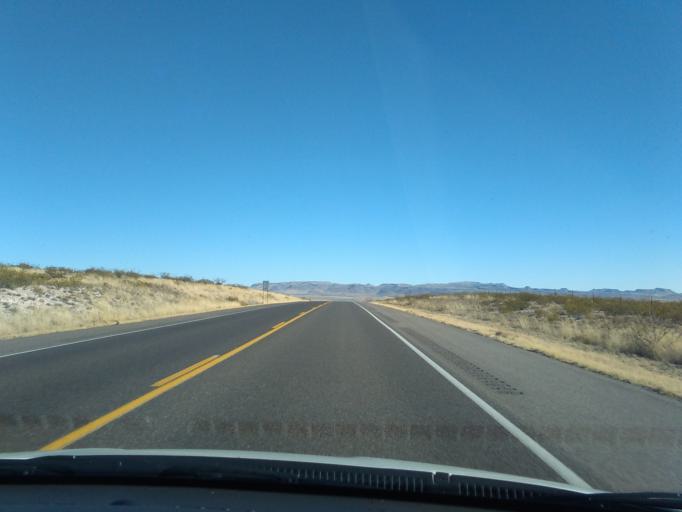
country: US
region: New Mexico
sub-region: Dona Ana County
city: Hatch
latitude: 32.5740
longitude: -107.4113
